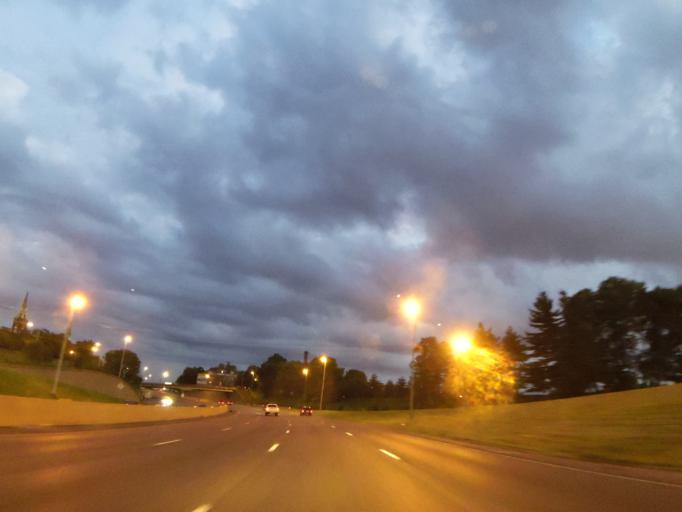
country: US
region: Missouri
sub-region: City of Saint Louis
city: St. Louis
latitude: 38.5966
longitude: -90.2162
